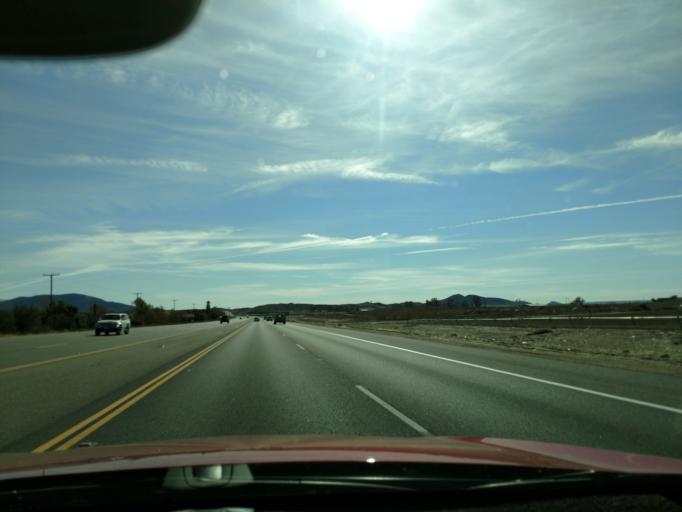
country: US
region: California
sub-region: Riverside County
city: Winchester
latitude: 33.6761
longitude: -117.0847
